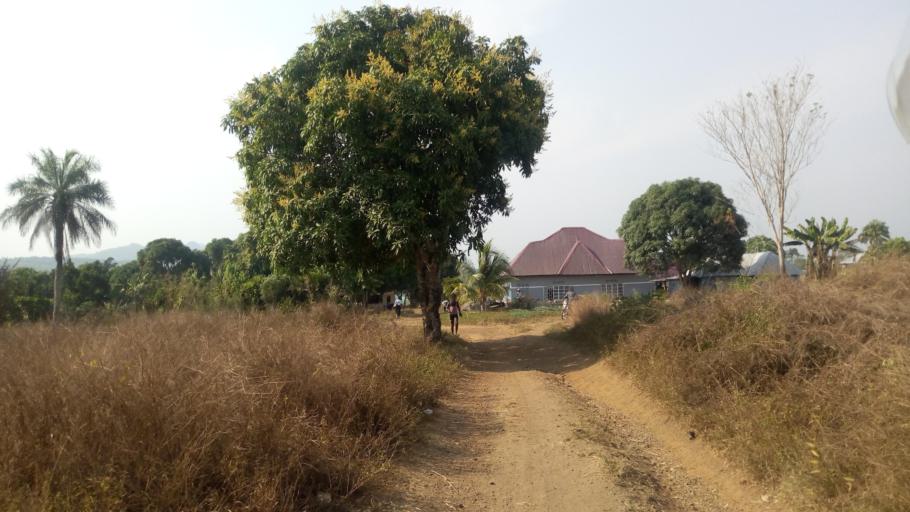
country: SL
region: Southern Province
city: Mogbwemo
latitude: 7.6169
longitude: -12.1801
